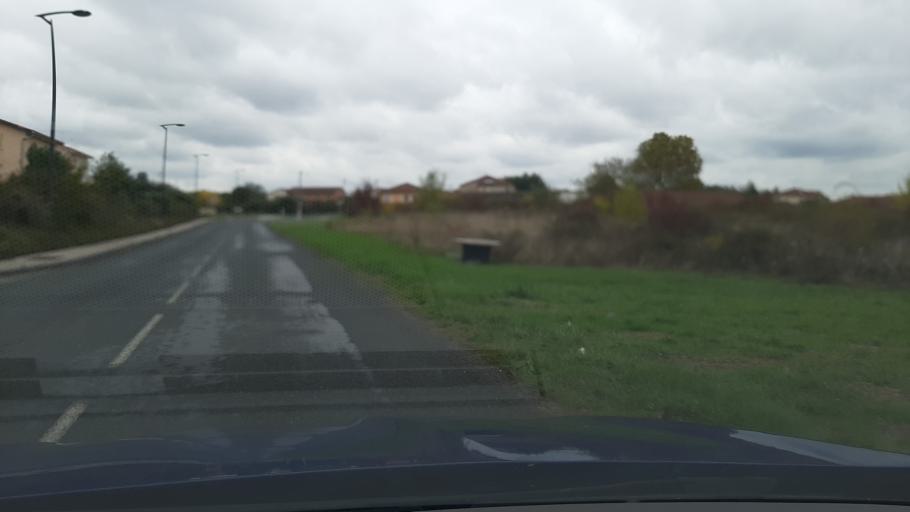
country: FR
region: Rhone-Alpes
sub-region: Departement du Rhone
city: Belleville
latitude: 46.1059
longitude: 4.7192
